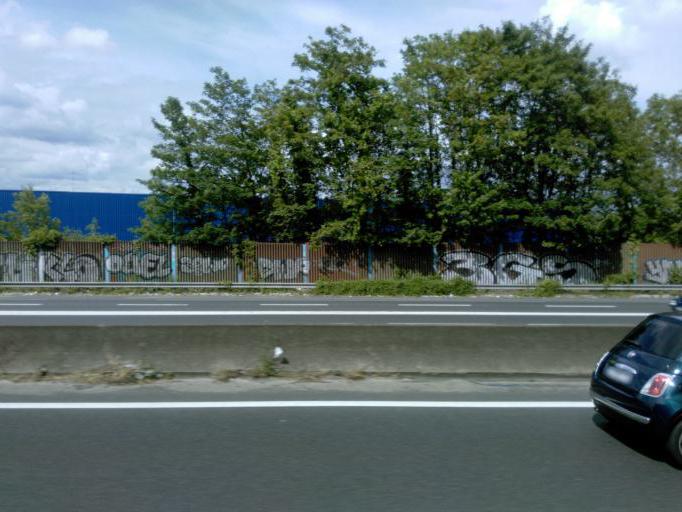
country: FR
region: Ile-de-France
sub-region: Departement du Val-d'Oise
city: Montigny-les-Cormeilles
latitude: 48.9848
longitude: 2.2152
